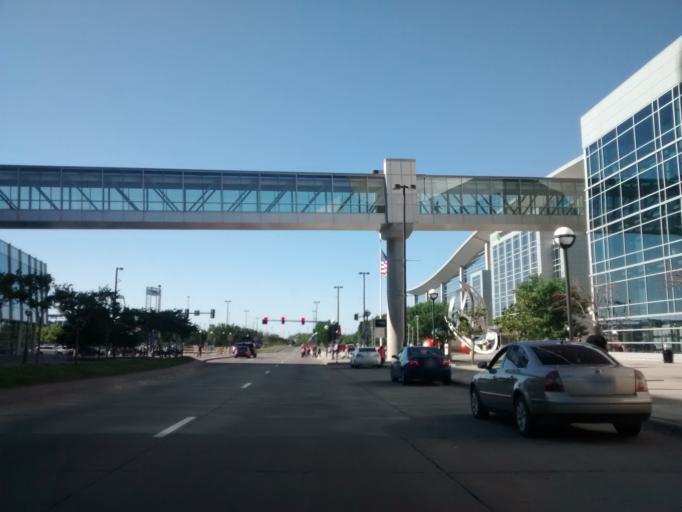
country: US
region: Nebraska
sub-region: Douglas County
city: Omaha
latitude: 41.2628
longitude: -95.9293
